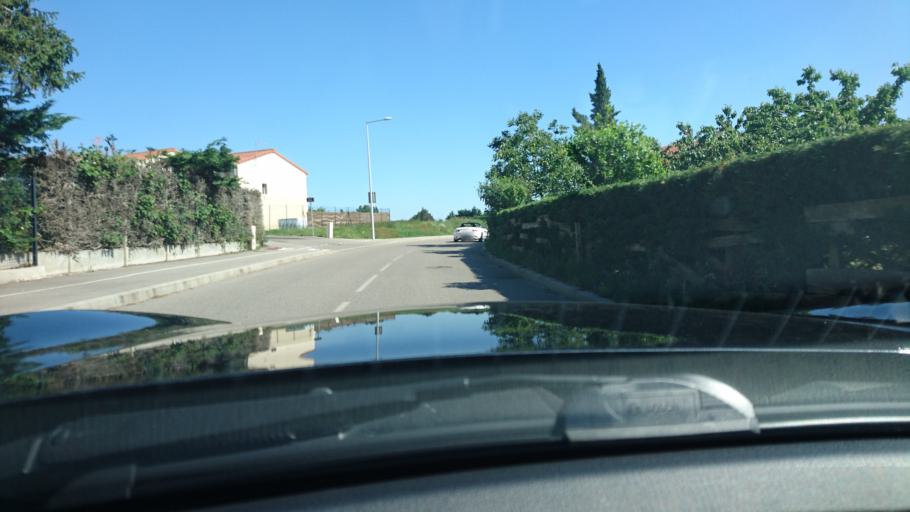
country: FR
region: Rhone-Alpes
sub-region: Departement du Rhone
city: Bessenay
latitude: 45.7789
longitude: 4.5474
